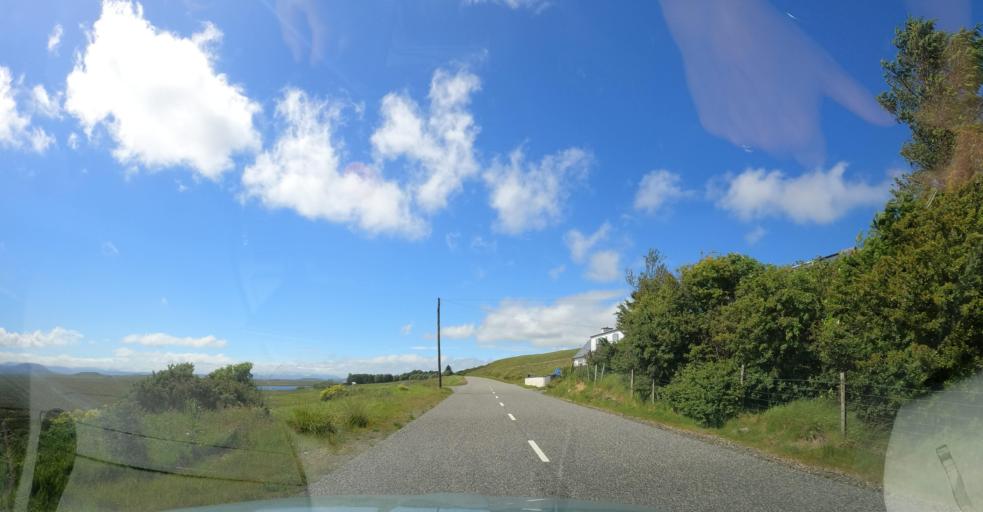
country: GB
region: Scotland
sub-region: Eilean Siar
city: Stornoway
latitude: 58.1654
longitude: -6.5530
